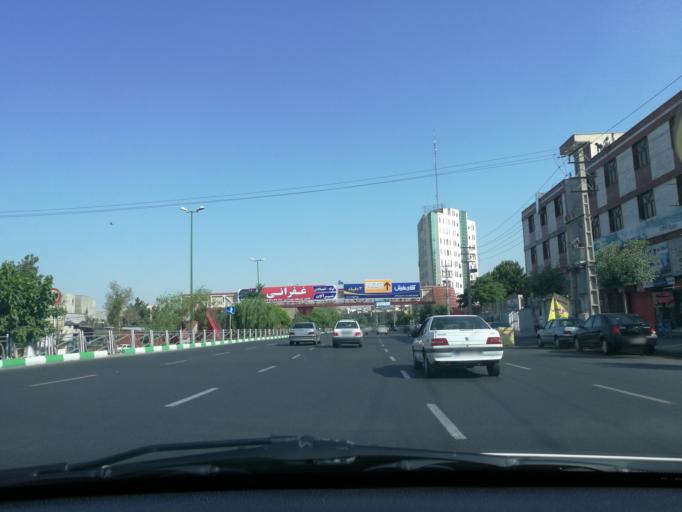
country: IR
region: Alborz
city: Karaj
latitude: 35.8371
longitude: 50.9926
